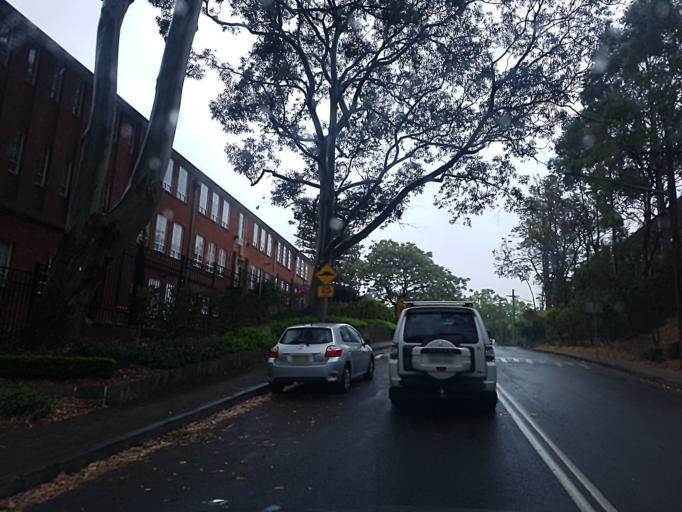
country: AU
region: New South Wales
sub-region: Ku-ring-gai
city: North Wahroonga
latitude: -33.7206
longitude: 151.1157
